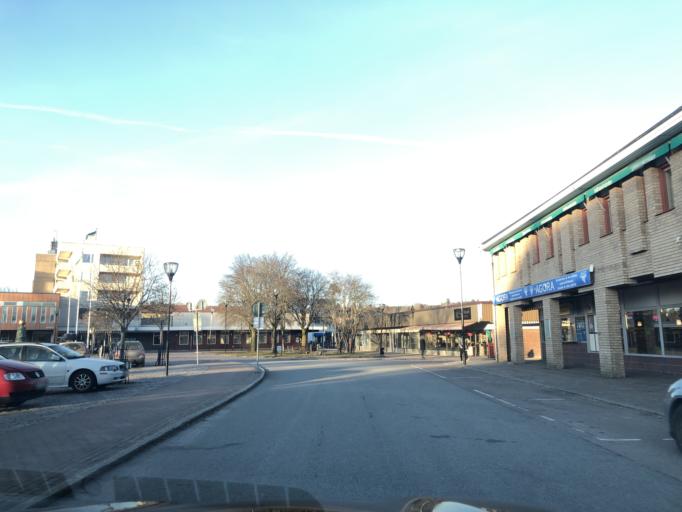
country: SE
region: Vaermland
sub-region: Filipstads Kommun
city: Filipstad
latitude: 59.7120
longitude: 14.1682
